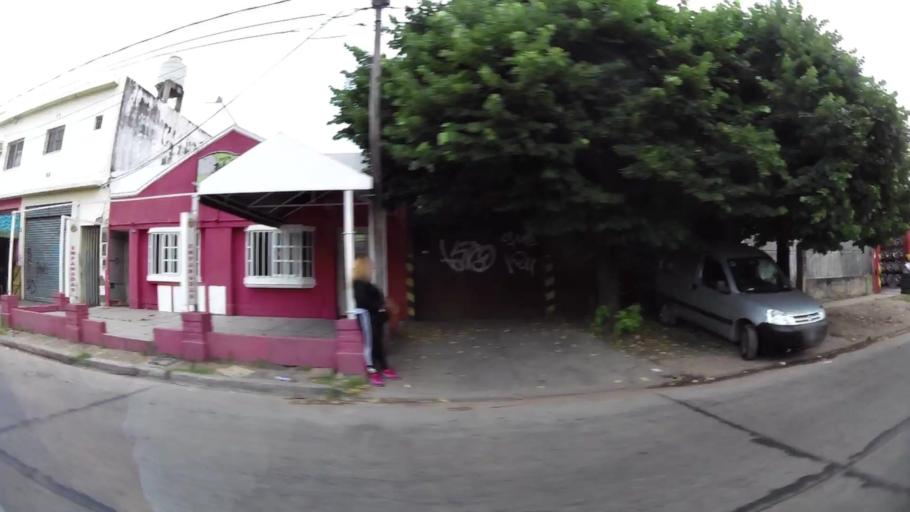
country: AR
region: Buenos Aires
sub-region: Partido de Moron
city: Moron
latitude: -34.6586
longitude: -58.5920
